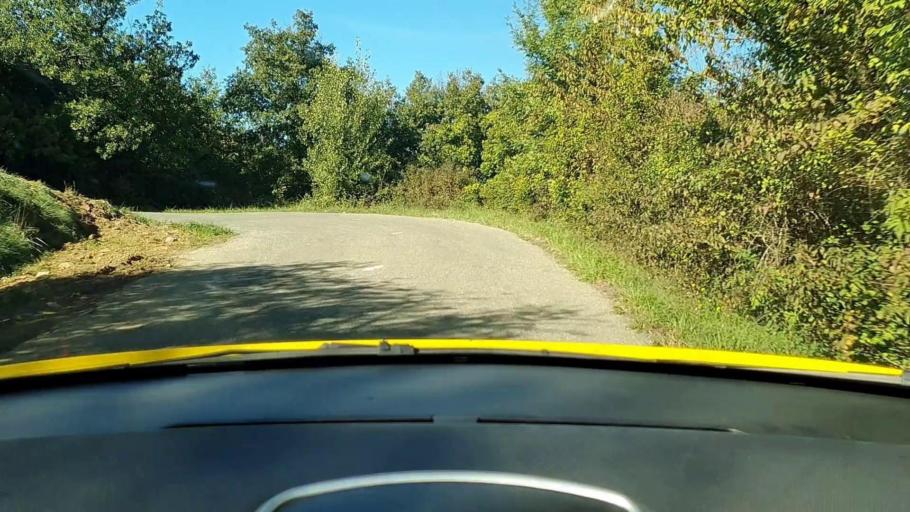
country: FR
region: Languedoc-Roussillon
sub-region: Departement du Gard
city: Aveze
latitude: 43.9624
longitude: 3.4254
